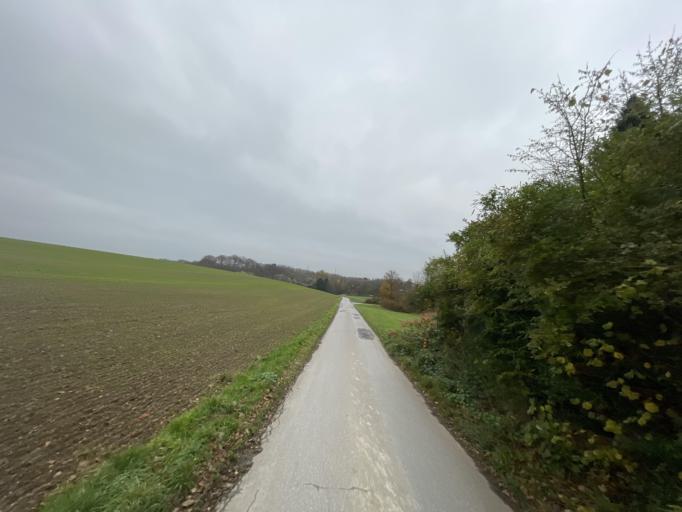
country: DE
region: North Rhine-Westphalia
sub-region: Regierungsbezirk Dusseldorf
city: Erkrath
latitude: 51.2618
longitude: 6.9118
